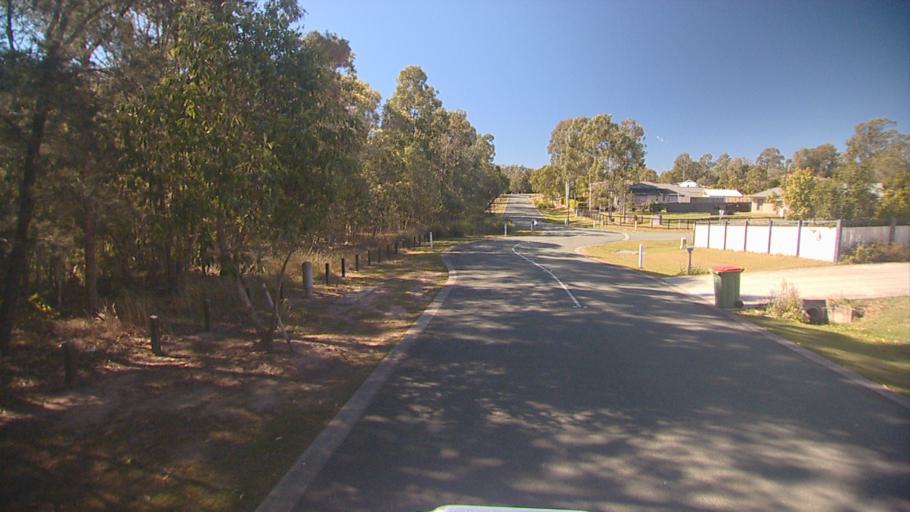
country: AU
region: Queensland
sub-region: Logan
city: North Maclean
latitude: -27.7556
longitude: 152.9652
